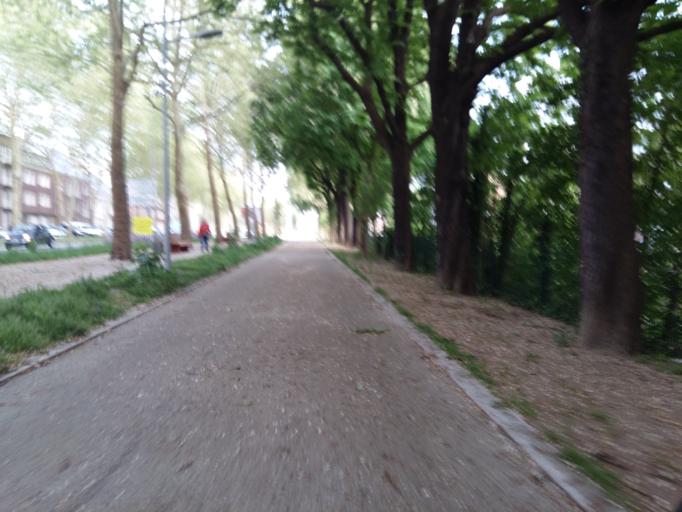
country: FR
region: Picardie
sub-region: Departement de la Somme
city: Amiens
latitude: 49.8916
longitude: 2.2883
